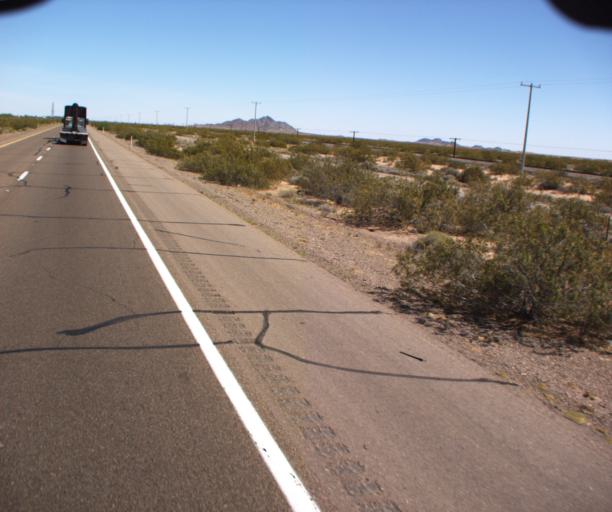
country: US
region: Arizona
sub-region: Yuma County
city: Wellton
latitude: 32.7860
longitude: -113.5687
